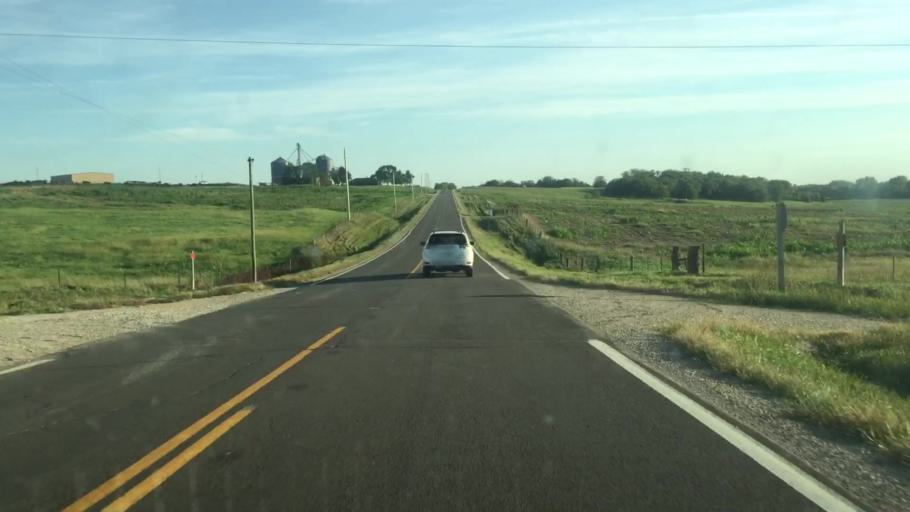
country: US
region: Kansas
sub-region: Brown County
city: Horton
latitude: 39.5803
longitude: -95.5270
